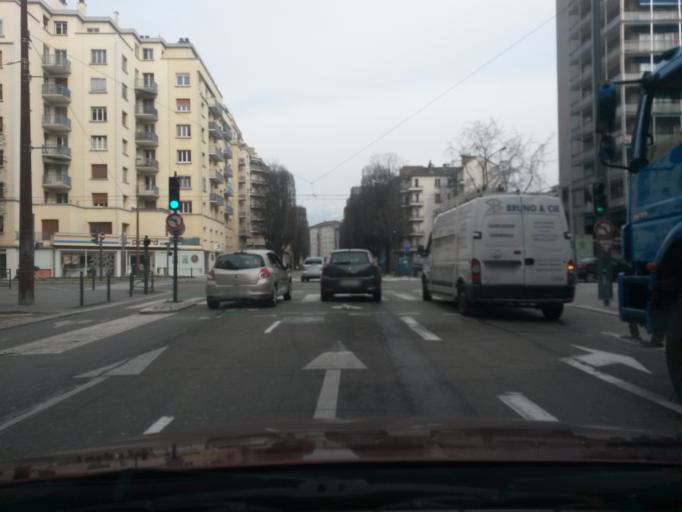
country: FR
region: Rhone-Alpes
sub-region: Departement de l'Isere
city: Grenoble
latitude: 45.1820
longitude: 5.7314
